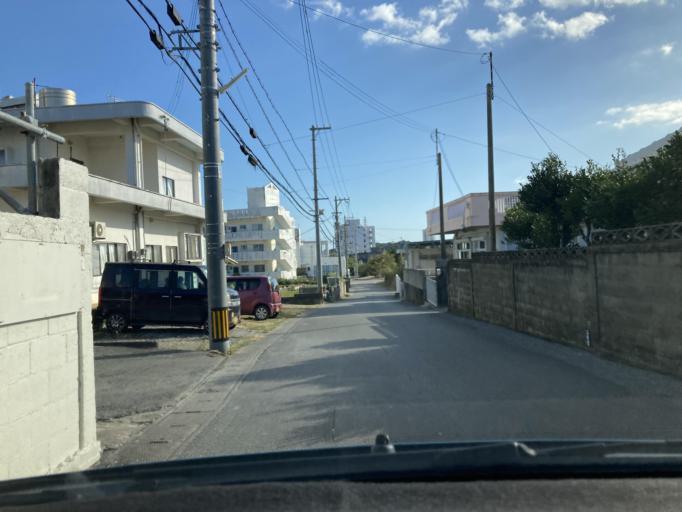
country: JP
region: Okinawa
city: Gushikawa
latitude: 26.3858
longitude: 127.8684
